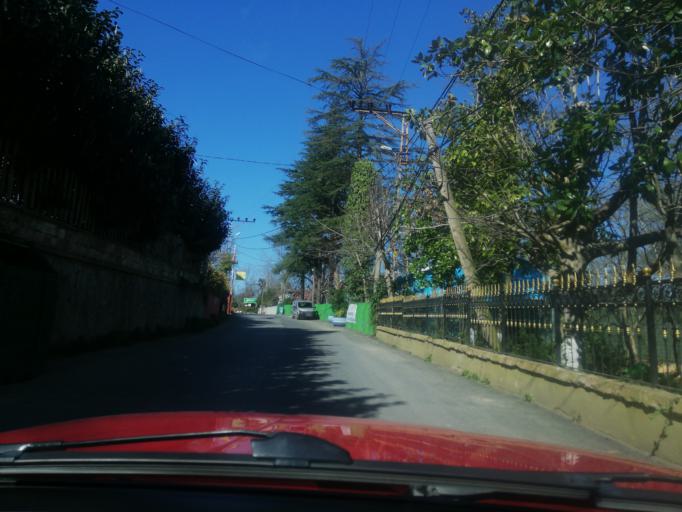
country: TR
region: Istanbul
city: Mahmut Sevket Pasa
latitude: 41.1125
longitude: 29.2113
